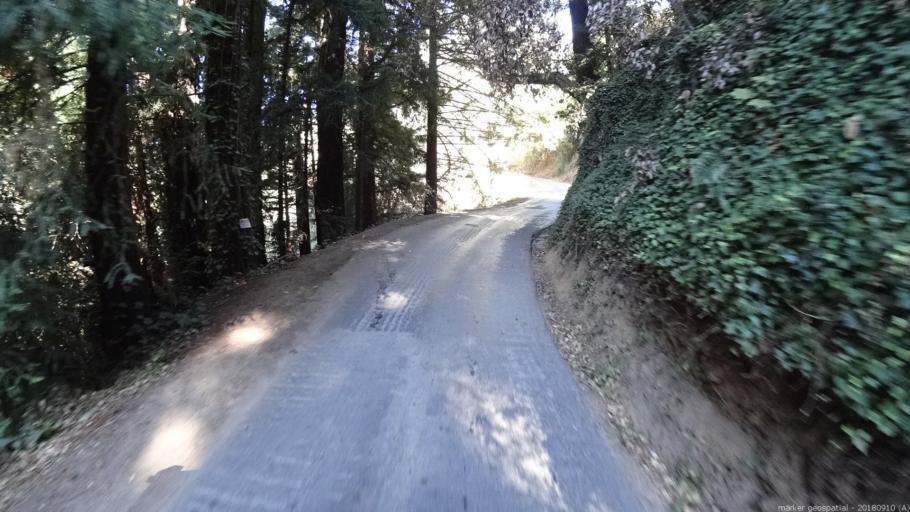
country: US
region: California
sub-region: Monterey County
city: Carmel Valley Village
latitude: 36.3970
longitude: -121.8801
